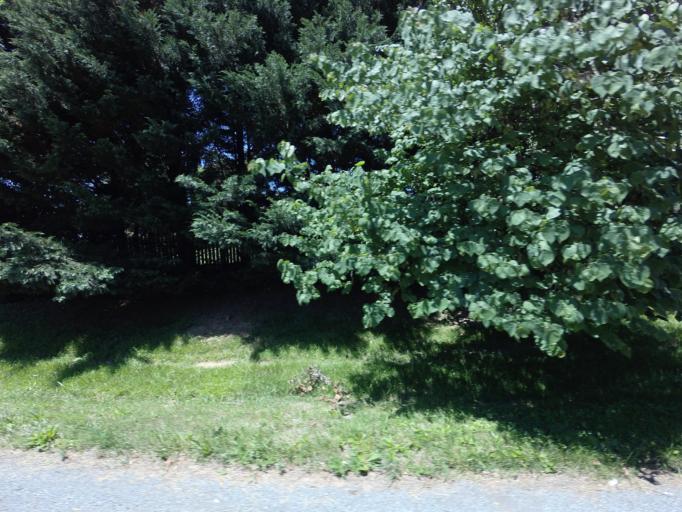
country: US
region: West Virginia
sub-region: Jefferson County
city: Ranson
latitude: 39.3220
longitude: -77.8365
